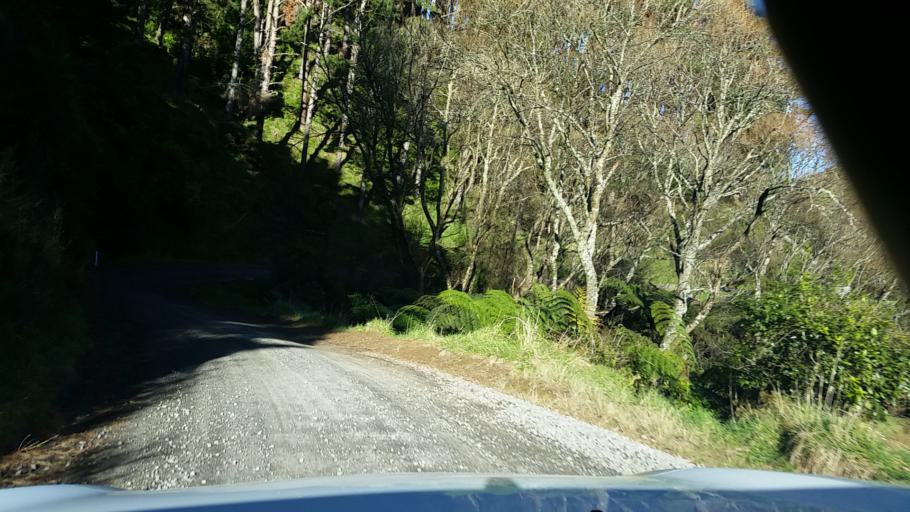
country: NZ
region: Taranaki
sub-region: South Taranaki District
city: Eltham
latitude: -39.5053
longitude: 174.3999
